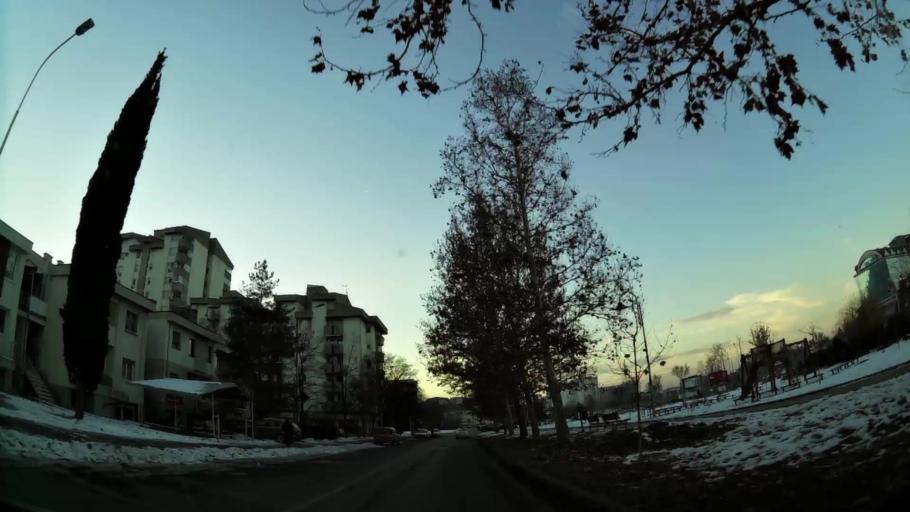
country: MK
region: Karpos
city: Skopje
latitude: 41.9956
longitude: 21.4047
